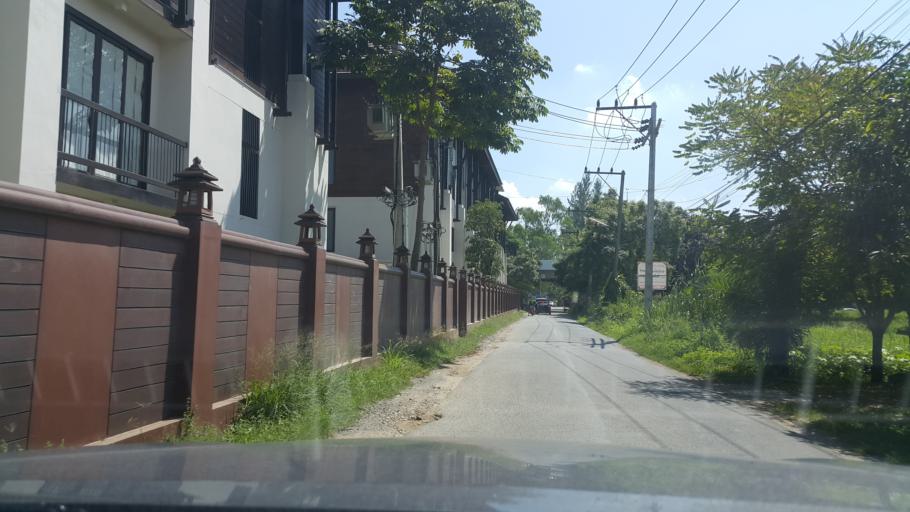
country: TH
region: Chiang Mai
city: Chiang Mai
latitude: 18.8451
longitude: 98.9842
